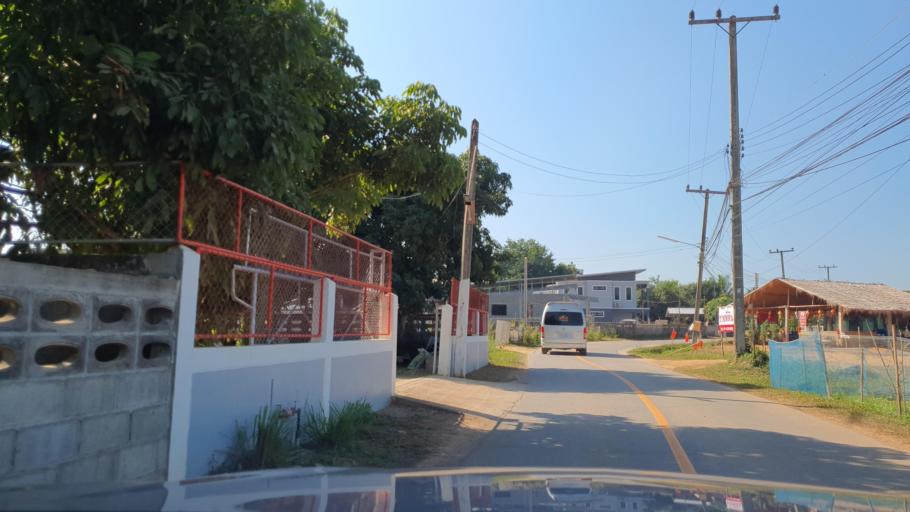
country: TH
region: Nan
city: Pua
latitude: 19.1657
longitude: 100.9309
